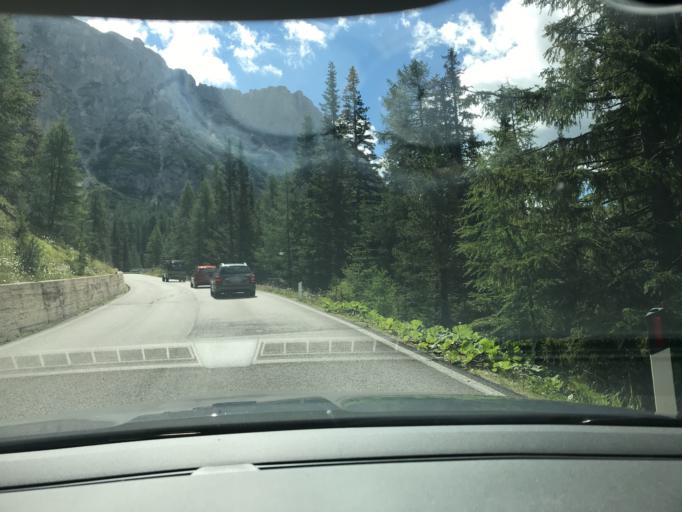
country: IT
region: Veneto
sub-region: Provincia di Belluno
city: Livinallongo del Col di Lana
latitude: 46.5418
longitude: 11.9791
